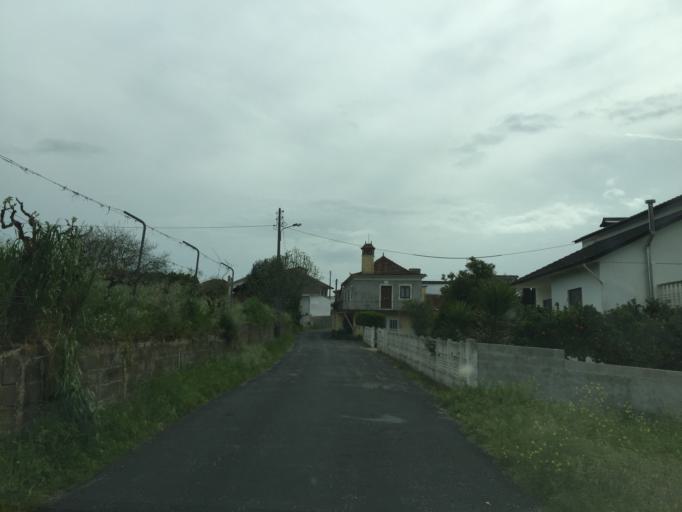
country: PT
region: Leiria
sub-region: Leiria
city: Caranguejeira
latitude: 39.7870
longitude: -8.7251
